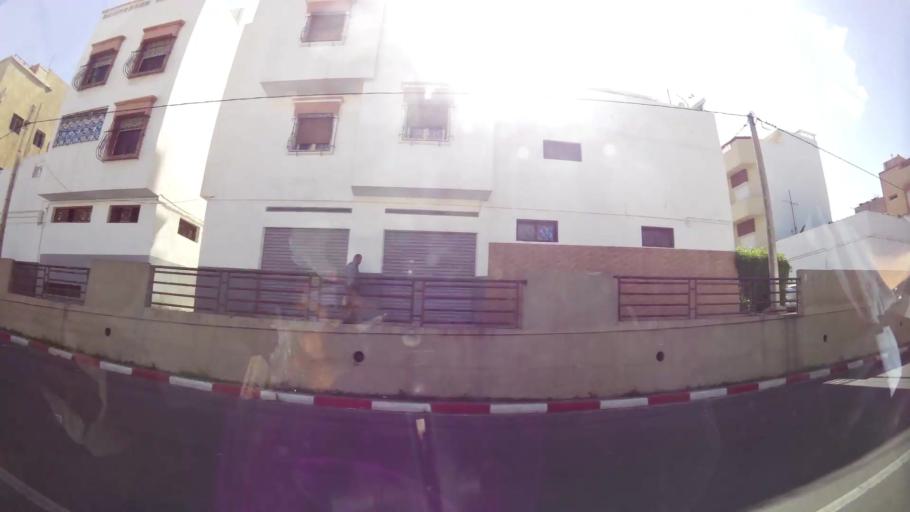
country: MA
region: Souss-Massa-Draa
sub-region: Agadir-Ida-ou-Tnan
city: Agadir
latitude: 30.4165
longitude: -9.5921
